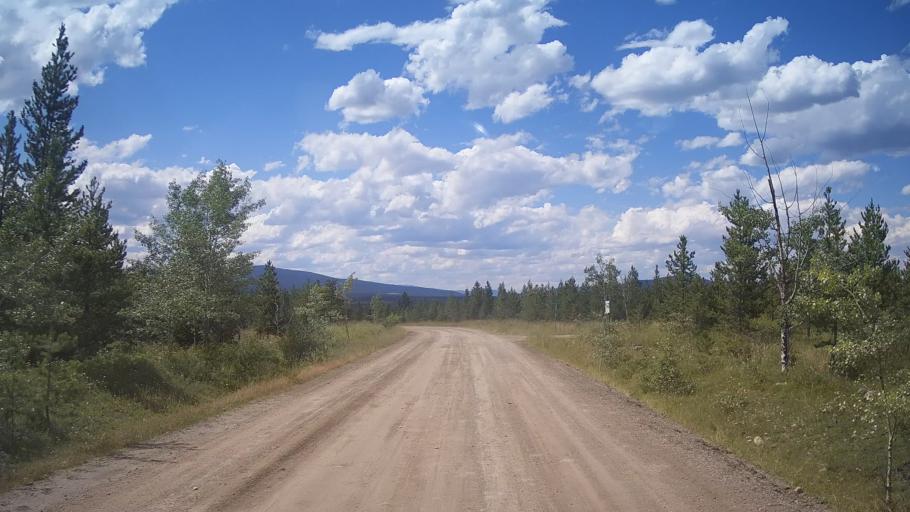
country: CA
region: British Columbia
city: Lillooet
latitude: 51.3415
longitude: -121.9274
